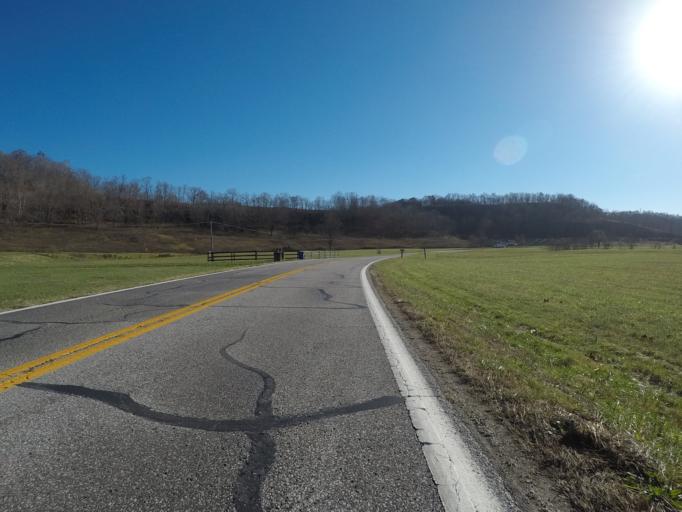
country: US
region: West Virginia
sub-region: Cabell County
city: Huntington
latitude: 38.4852
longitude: -82.4500
